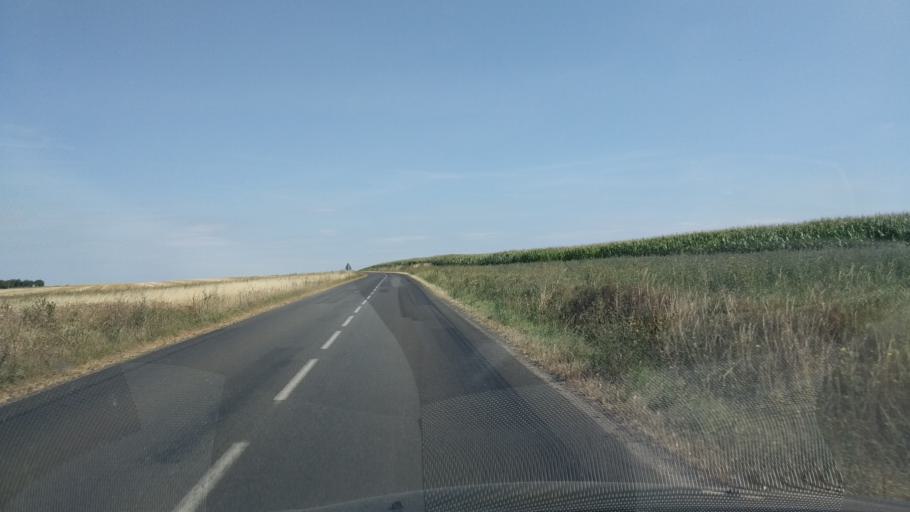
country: FR
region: Poitou-Charentes
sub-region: Departement de la Vienne
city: Cisse
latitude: 46.6603
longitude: 0.2107
